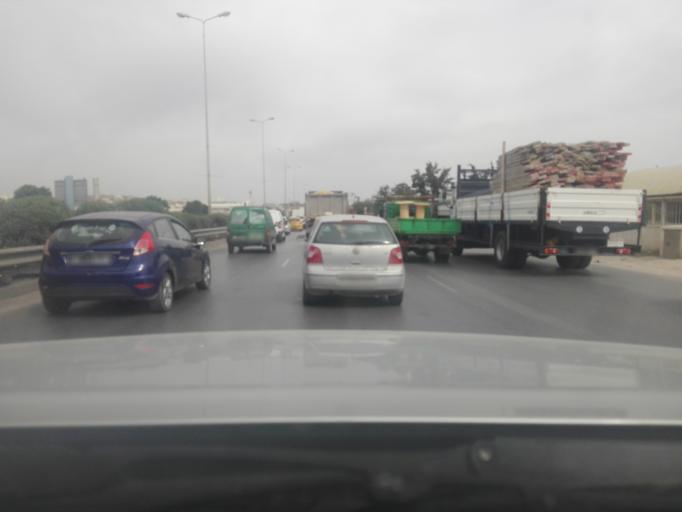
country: TN
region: Bin 'Arus
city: Ben Arous
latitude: 36.7569
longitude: 10.2010
